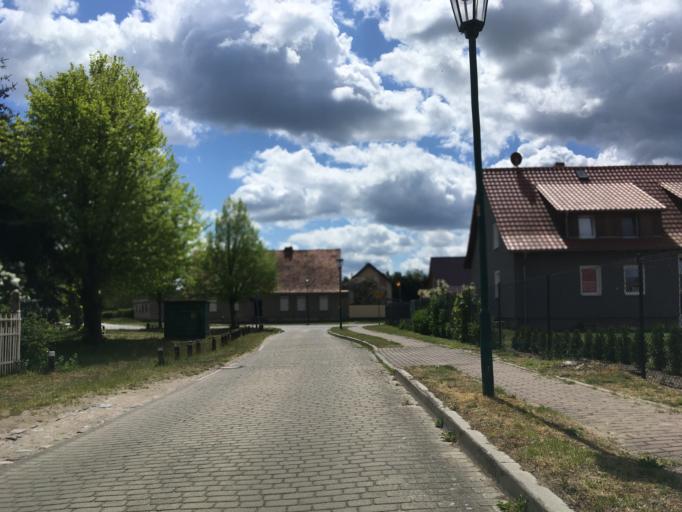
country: DE
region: Brandenburg
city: Liebenwalde
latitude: 52.8814
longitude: 13.4445
